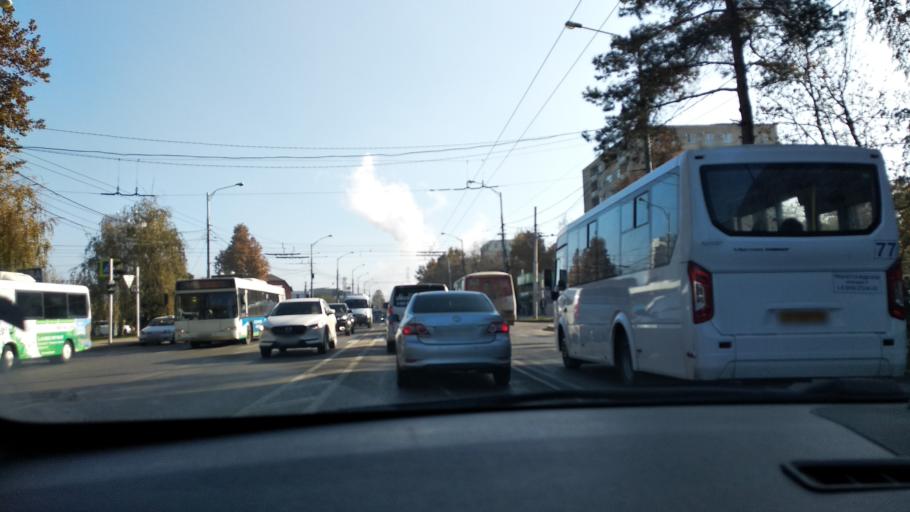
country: RU
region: Krasnodarskiy
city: Pashkovskiy
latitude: 45.0233
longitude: 39.0426
